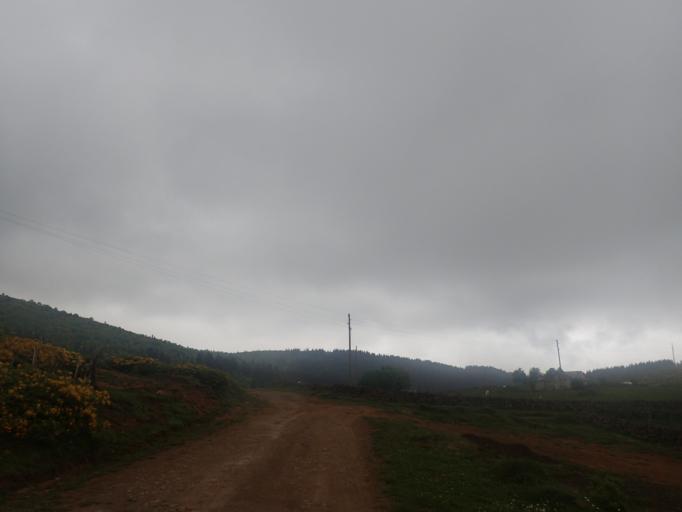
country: TR
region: Ordu
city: Topcam
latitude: 40.6672
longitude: 37.9266
